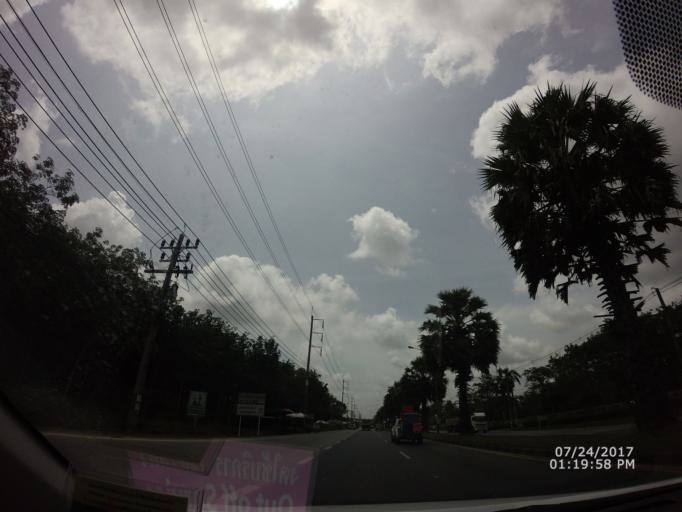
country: TH
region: Phuket
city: Thalang
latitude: 8.0644
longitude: 98.3416
